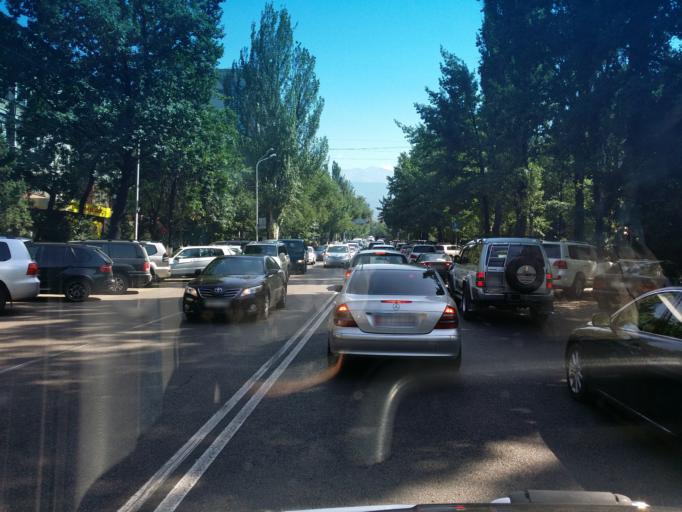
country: KZ
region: Almaty Qalasy
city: Almaty
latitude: 43.2231
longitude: 76.9627
